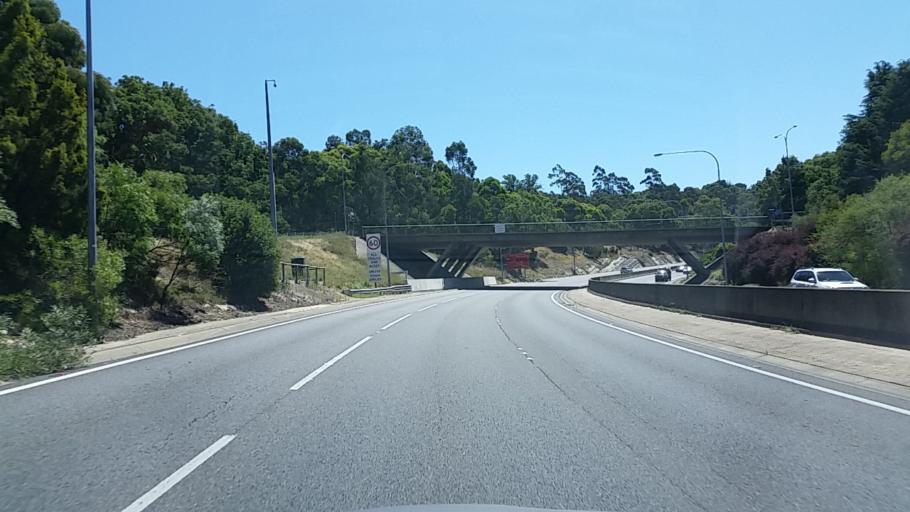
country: AU
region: South Australia
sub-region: Adelaide Hills
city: Crafers
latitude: -34.9984
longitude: 138.7035
